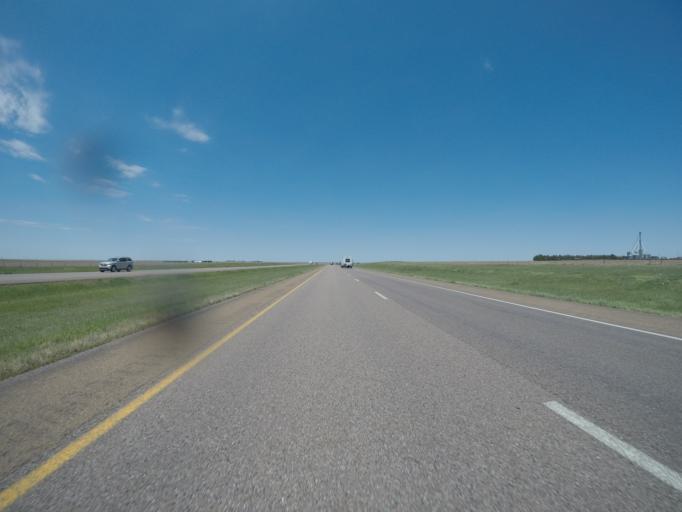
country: US
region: Kansas
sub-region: Thomas County
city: Colby
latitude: 39.3157
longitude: -100.9834
